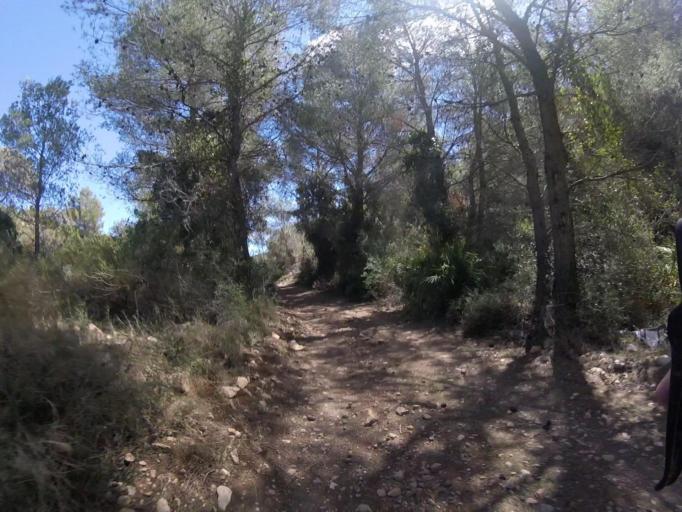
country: ES
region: Valencia
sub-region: Provincia de Castello
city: Orpesa/Oropesa del Mar
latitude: 40.1673
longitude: 0.1299
